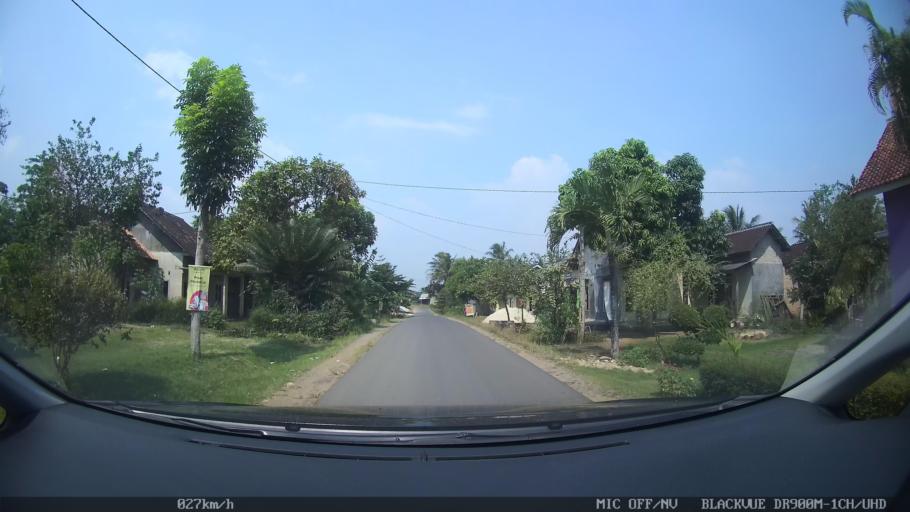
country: ID
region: Lampung
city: Natar
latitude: -5.3044
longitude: 105.2363
